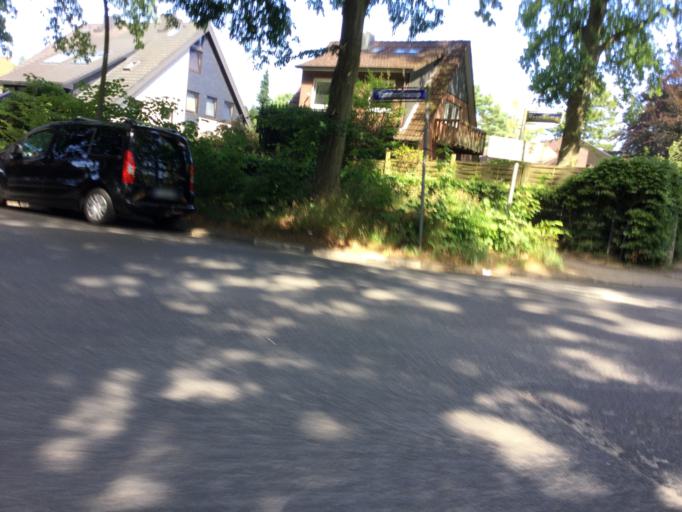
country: DE
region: Hamburg
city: Bergstedt
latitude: 53.6408
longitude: 10.1490
